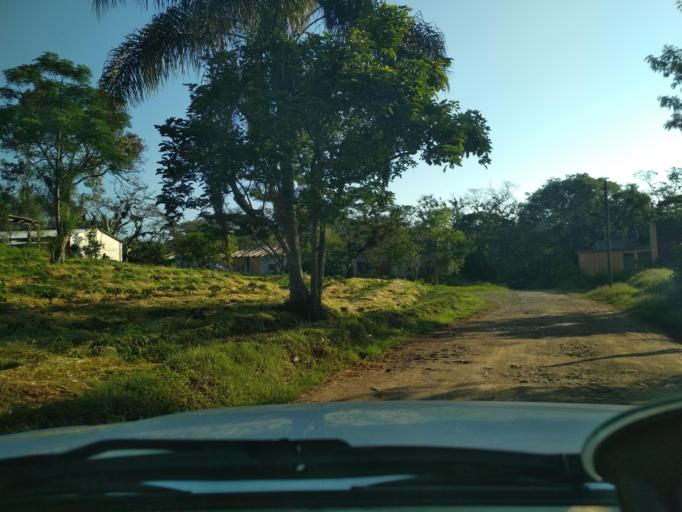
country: MX
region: Veracruz
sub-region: Fortin
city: Fraccionamiento Villas de la Llave
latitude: 18.9265
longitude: -96.9918
